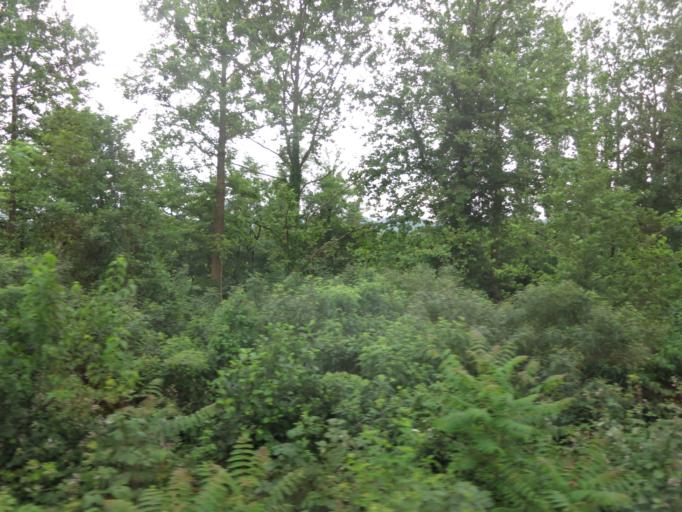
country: GE
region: Guria
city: Lanchkhuti
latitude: 42.0810
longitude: 41.9289
